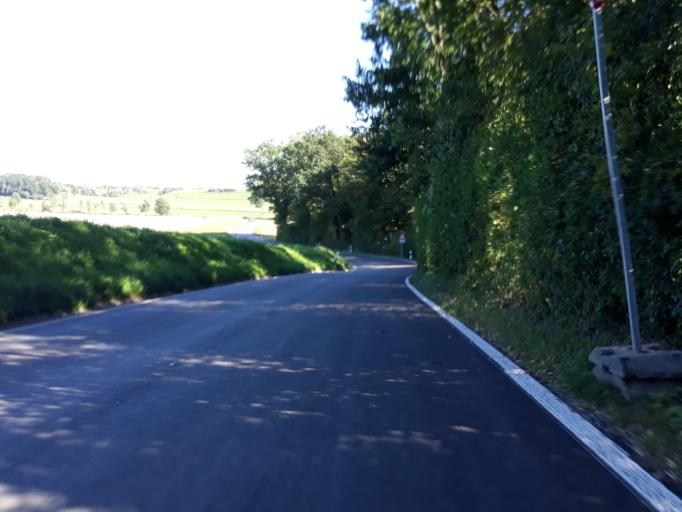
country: DE
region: Baden-Wuerttemberg
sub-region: Regierungsbezirk Stuttgart
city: Altdorf
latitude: 48.6504
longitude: 8.9805
